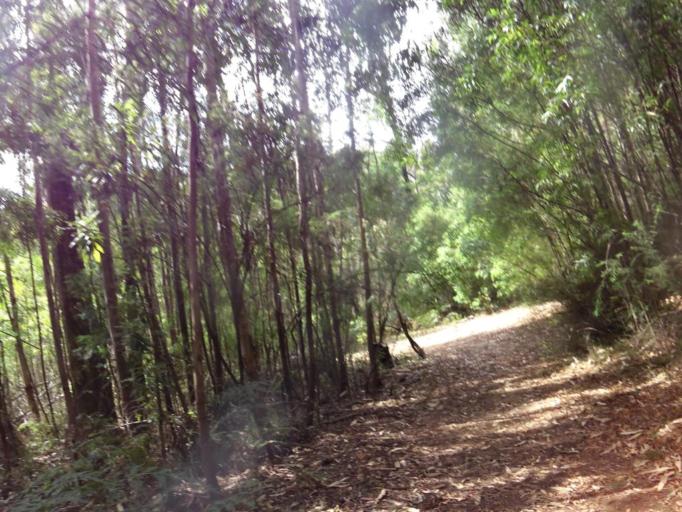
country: AU
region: Victoria
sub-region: Murrindindi
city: Alexandra
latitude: -37.3993
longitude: 145.5751
